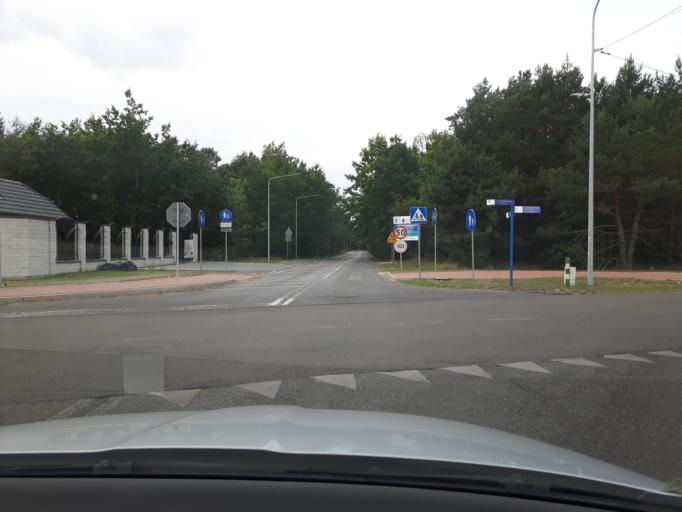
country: PL
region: Masovian Voivodeship
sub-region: Powiat legionowski
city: Wieliszew
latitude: 52.4616
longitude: 20.9442
